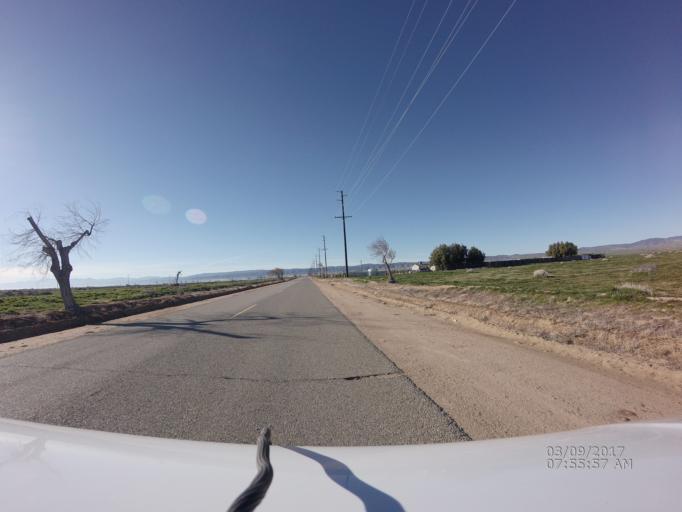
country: US
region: California
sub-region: Los Angeles County
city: Leona Valley
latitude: 34.7830
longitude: -118.3258
